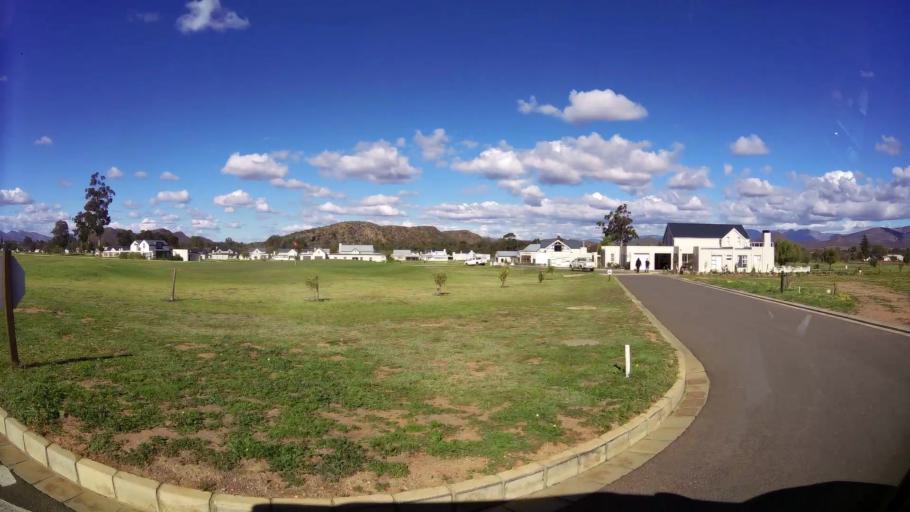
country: ZA
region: Western Cape
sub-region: Cape Winelands District Municipality
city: Ashton
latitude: -33.8140
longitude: 19.8453
